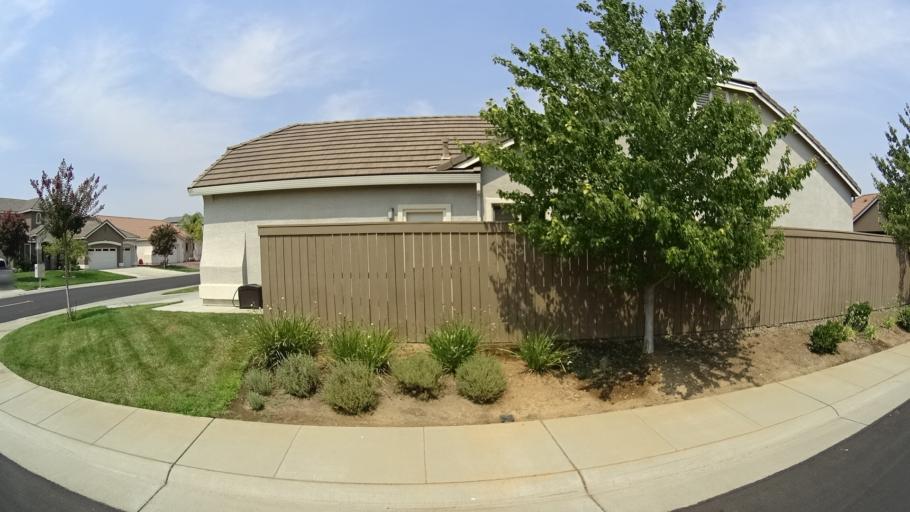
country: US
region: California
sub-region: Sacramento County
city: Elk Grove
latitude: 38.3953
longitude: -121.4017
